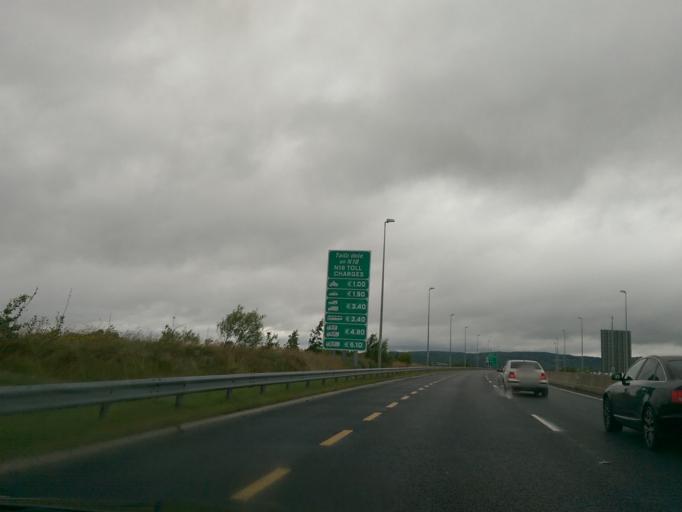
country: IE
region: Munster
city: Moyross
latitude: 52.6628
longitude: -8.6962
